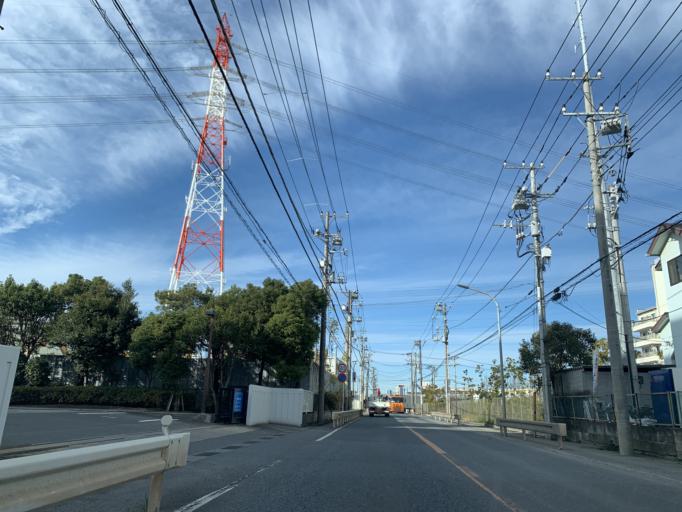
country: JP
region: Chiba
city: Funabashi
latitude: 35.6907
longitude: 139.9470
